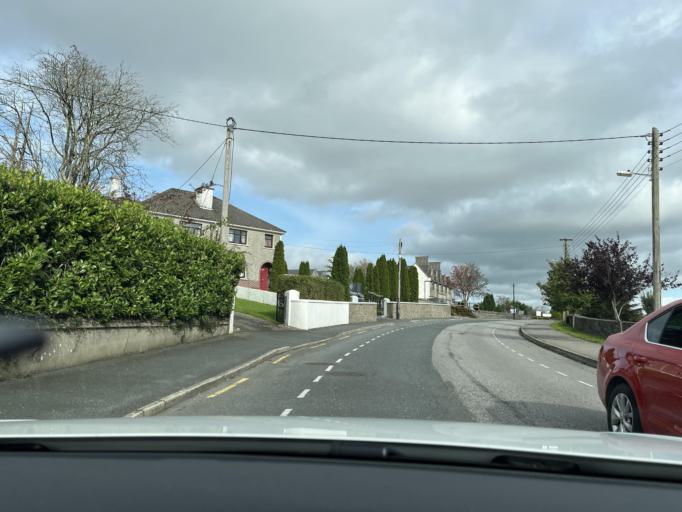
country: IE
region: Connaught
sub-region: County Leitrim
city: Carrick-on-Shannon
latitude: 53.9494
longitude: -8.0868
